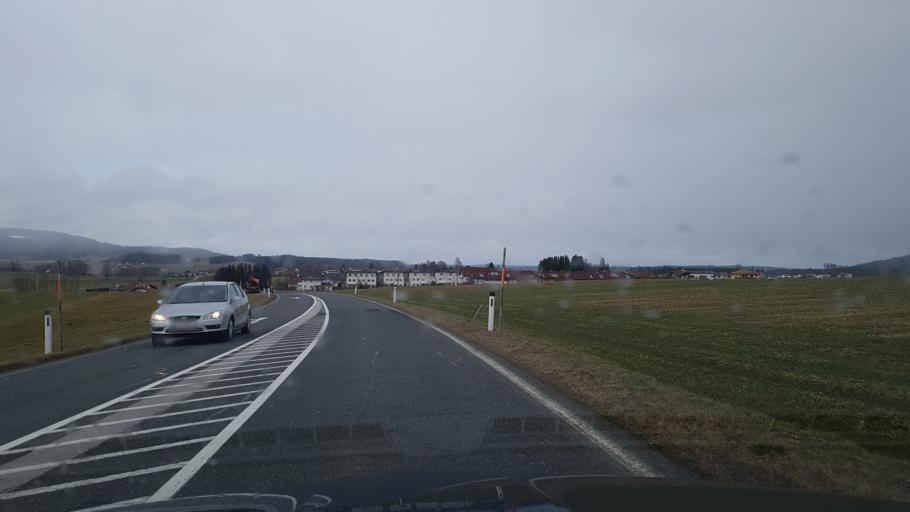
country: AT
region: Salzburg
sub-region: Politischer Bezirk Salzburg-Umgebung
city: Neumarkt am Wallersee
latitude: 47.9278
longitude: 13.2210
